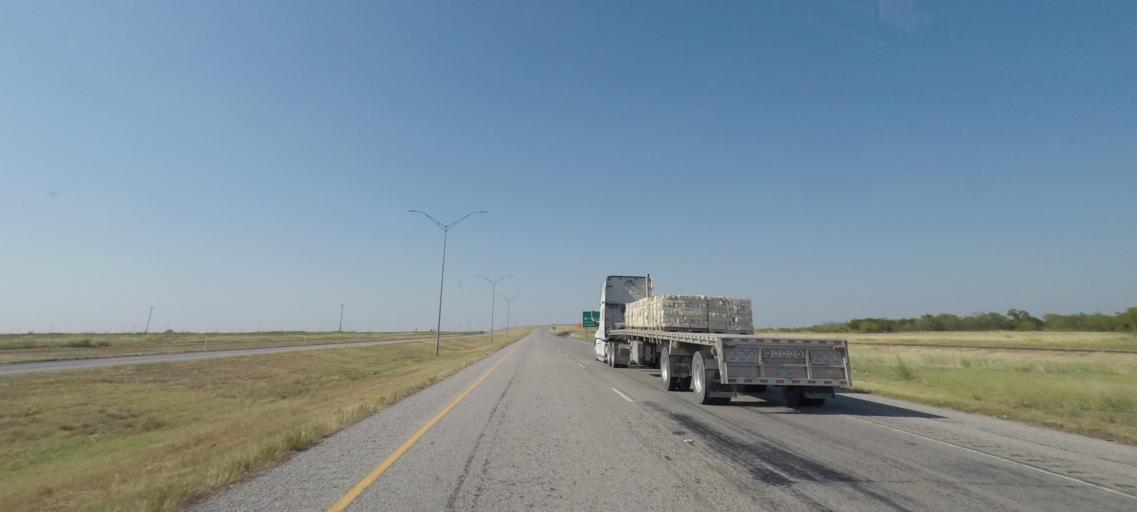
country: US
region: Texas
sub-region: Baylor County
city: Seymour
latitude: 33.6086
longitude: -99.2427
